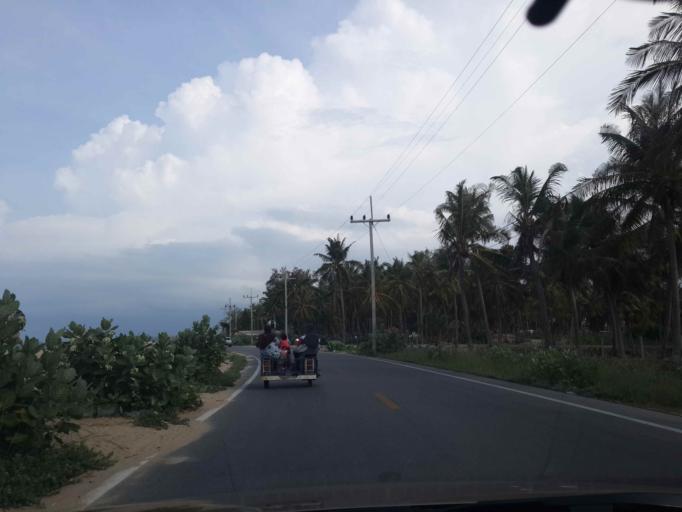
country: TH
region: Pattani
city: Yaring
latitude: 6.9168
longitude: 101.3370
